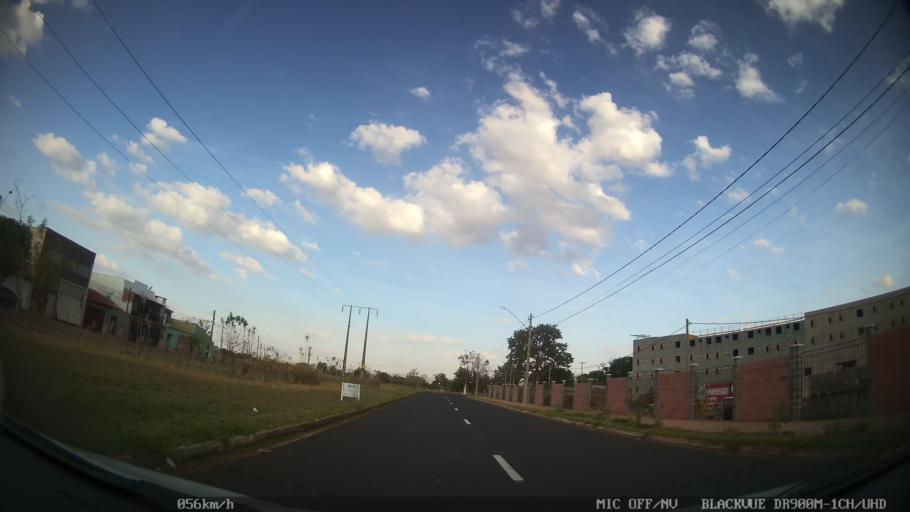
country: BR
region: Sao Paulo
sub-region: Ribeirao Preto
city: Ribeirao Preto
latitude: -21.1953
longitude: -47.7348
